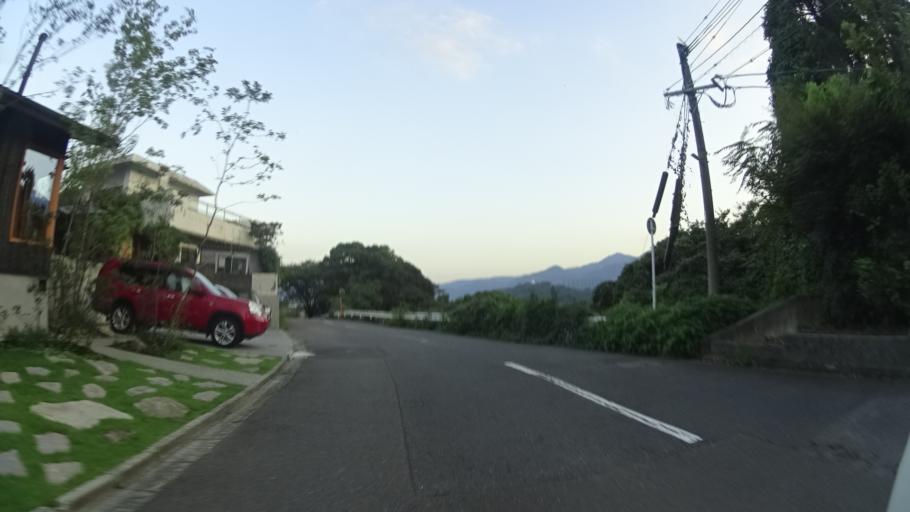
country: JP
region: Oita
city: Beppu
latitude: 33.3168
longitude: 131.4846
